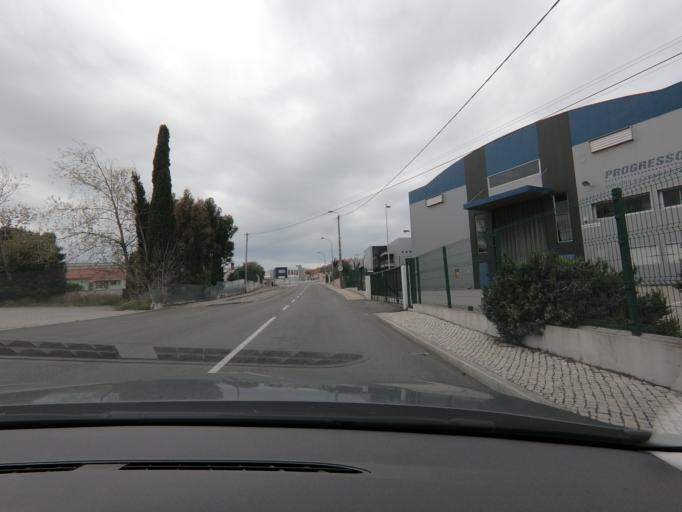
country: PT
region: Lisbon
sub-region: Cascais
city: Sao Domingos de Rana
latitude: 38.7241
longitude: -9.3286
